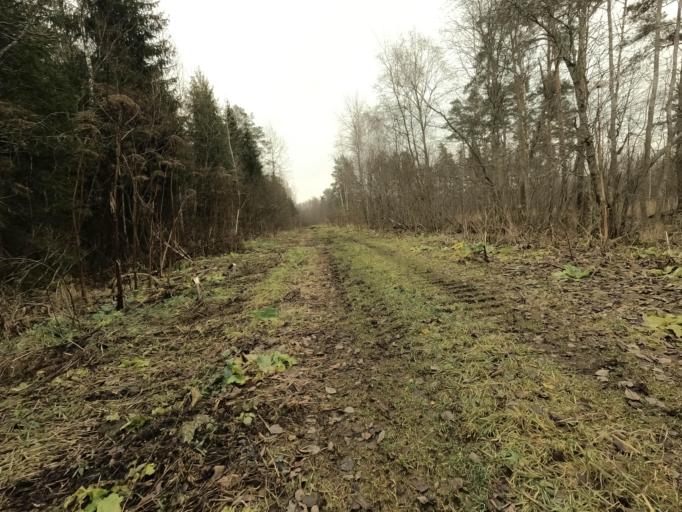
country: RU
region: Leningrad
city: Nurma
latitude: 59.6063
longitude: 31.1979
